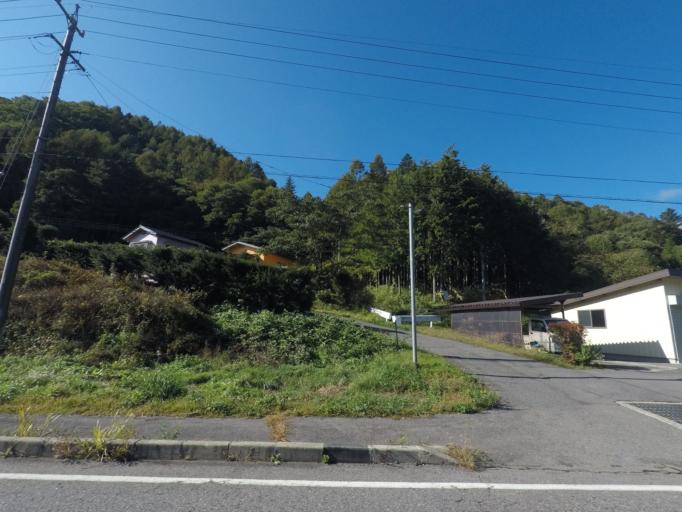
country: JP
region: Nagano
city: Tatsuno
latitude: 35.9681
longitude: 137.7625
